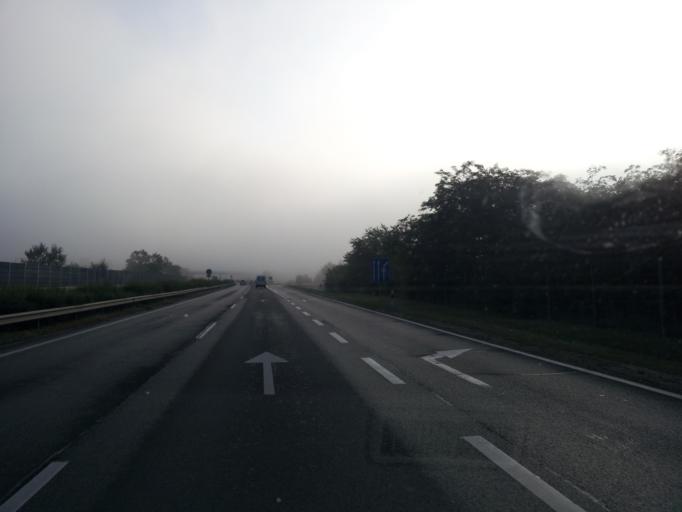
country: HU
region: Pest
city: Bag
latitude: 47.6330
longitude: 19.4685
